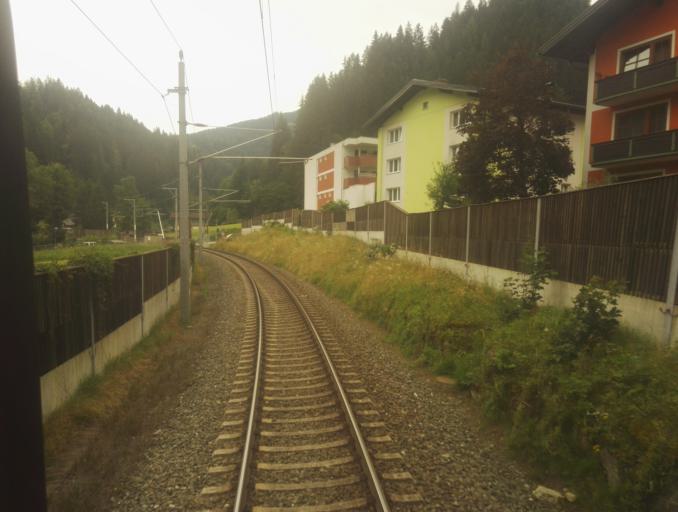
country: AT
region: Salzburg
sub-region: Politischer Bezirk Sankt Johann im Pongau
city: Huttau
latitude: 47.4142
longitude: 13.3092
